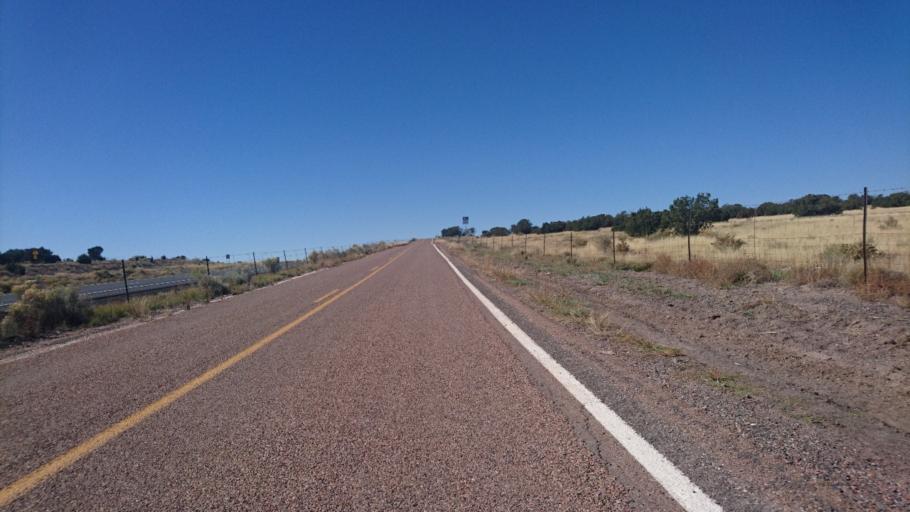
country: US
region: Arizona
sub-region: Apache County
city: Houck
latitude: 35.2819
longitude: -109.1957
